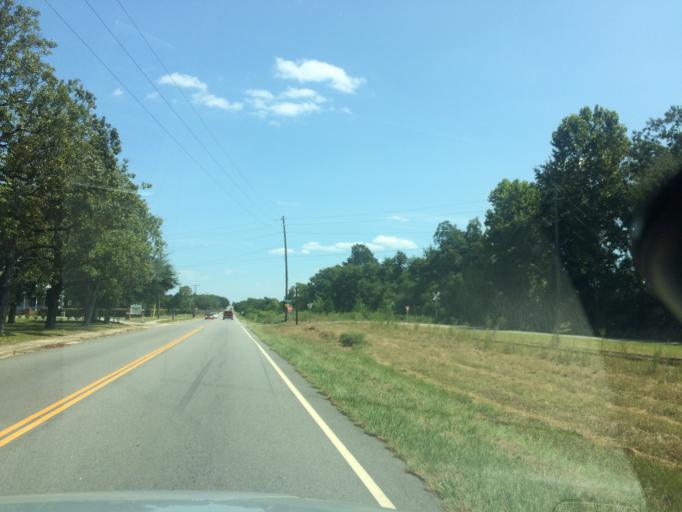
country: US
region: South Carolina
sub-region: Aiken County
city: Aiken
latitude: 33.5270
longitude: -81.6323
